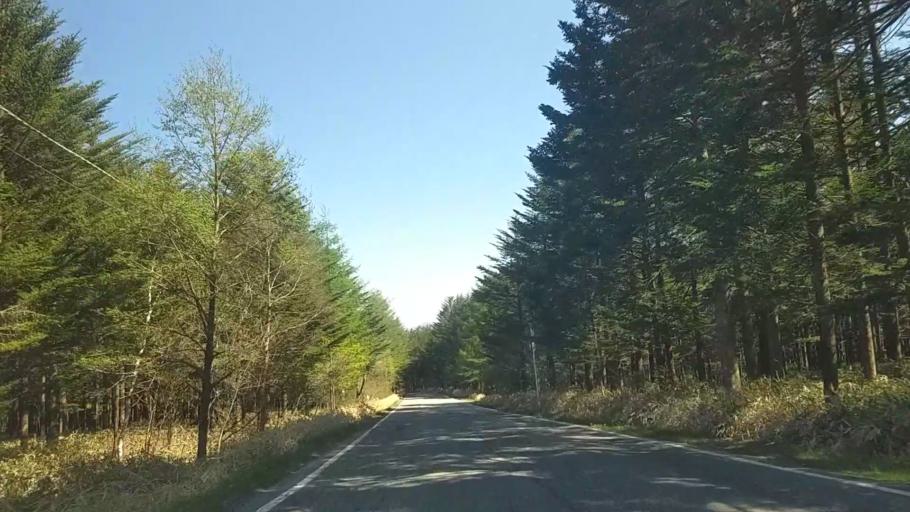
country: JP
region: Yamanashi
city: Nirasaki
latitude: 35.9426
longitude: 138.4199
